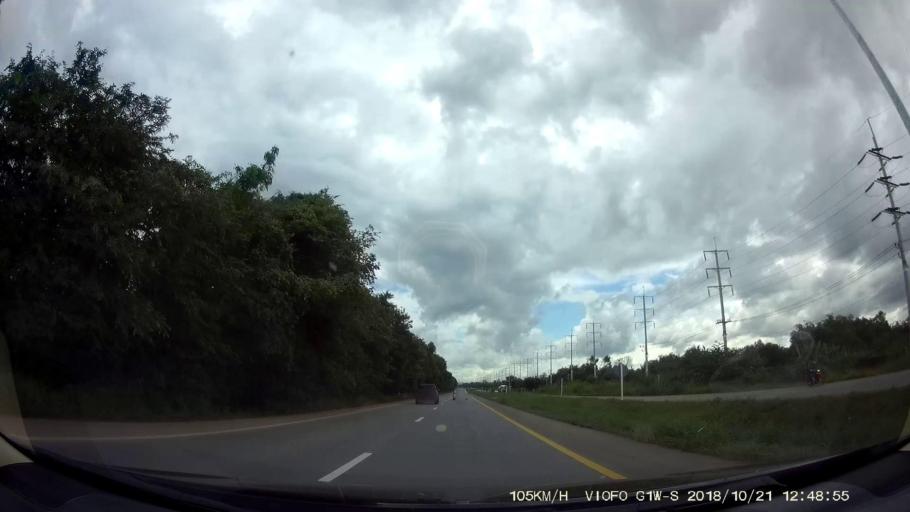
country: TH
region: Nakhon Ratchasima
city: Amphoe Sikhiu
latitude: 14.9048
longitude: 101.6841
